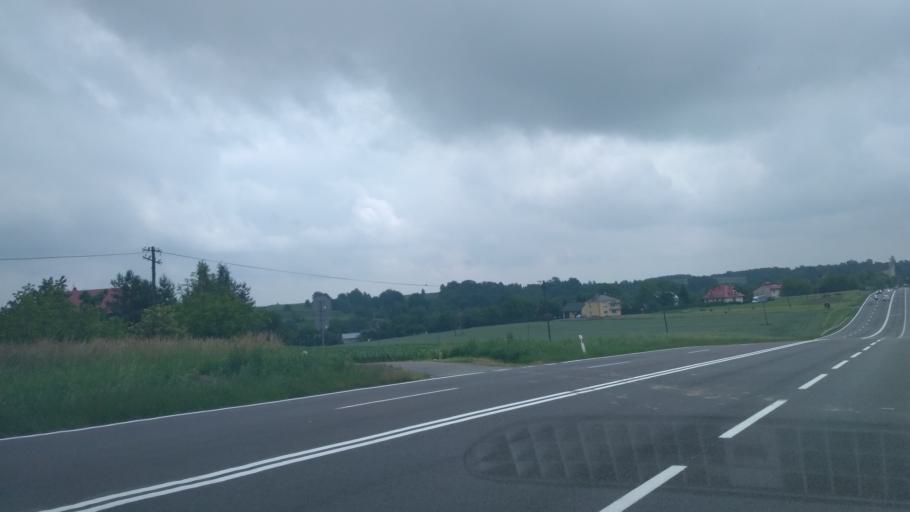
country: PL
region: Subcarpathian Voivodeship
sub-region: Powiat przeworski
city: Rozborz
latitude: 50.0463
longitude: 22.5415
